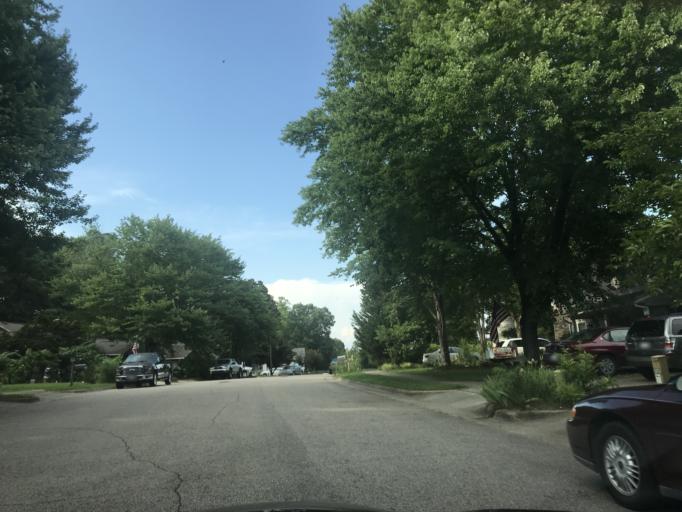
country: US
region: North Carolina
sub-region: Wake County
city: Raleigh
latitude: 35.8312
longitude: -78.5866
